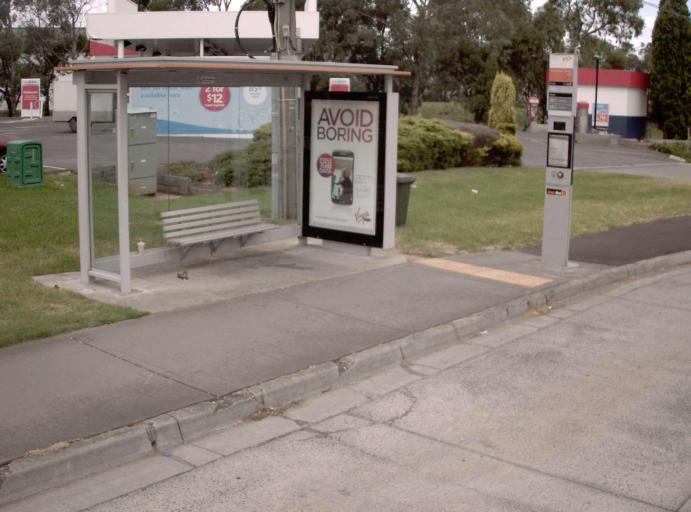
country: AU
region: Victoria
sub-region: Knox
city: Scoresby
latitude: -37.8998
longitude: 145.2336
